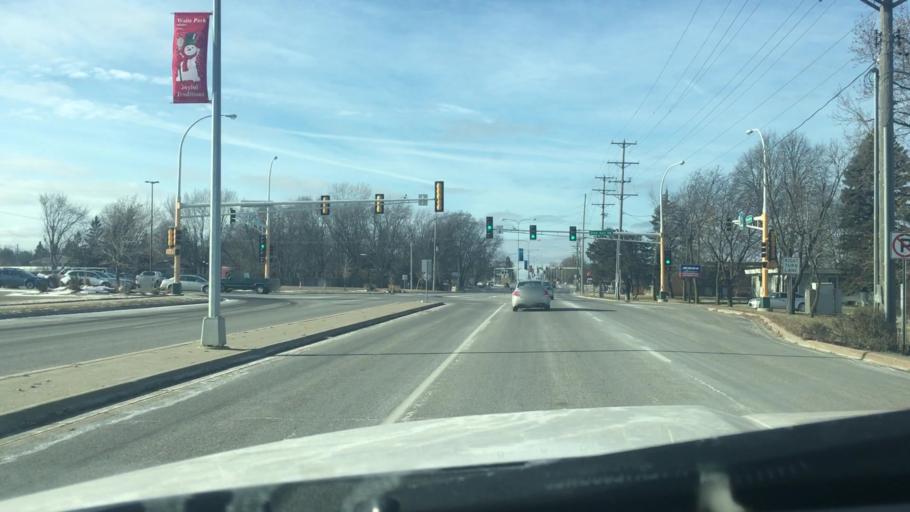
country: US
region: Minnesota
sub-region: Stearns County
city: Waite Park
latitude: 45.5588
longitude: -94.2090
